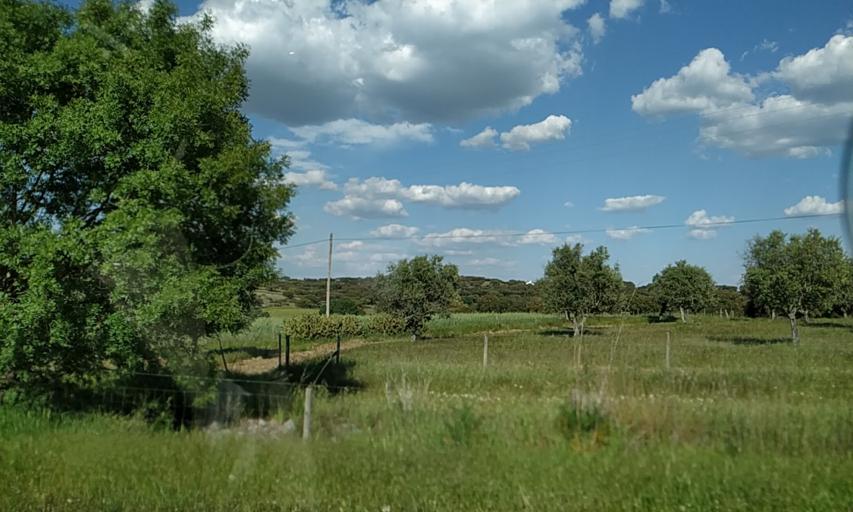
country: PT
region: Evora
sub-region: Estremoz
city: Estremoz
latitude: 38.8749
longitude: -7.5631
